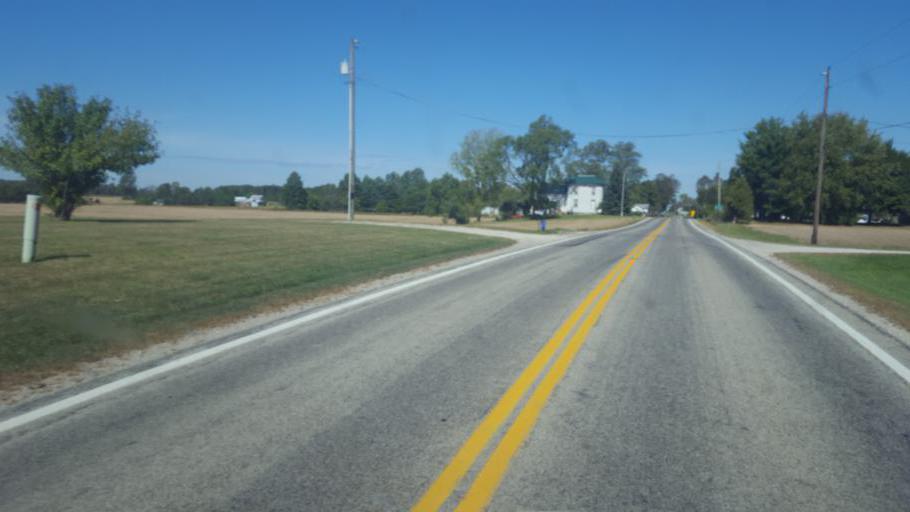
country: US
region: Ohio
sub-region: Crawford County
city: Bucyrus
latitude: 40.9025
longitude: -83.0167
